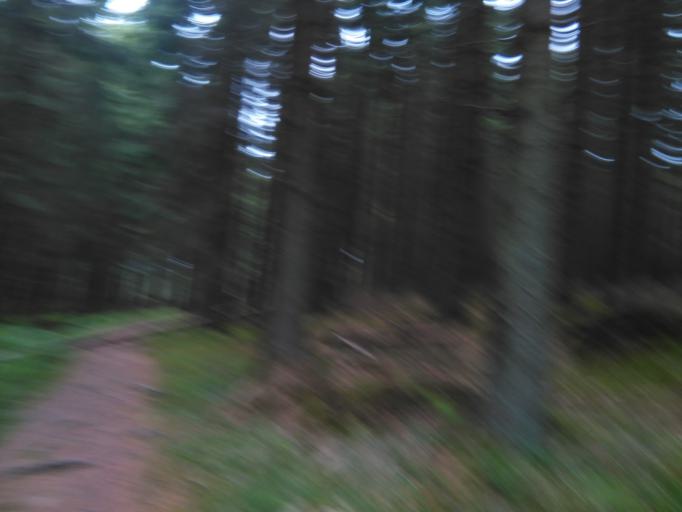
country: DK
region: Capital Region
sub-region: Bornholm Kommune
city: Akirkeby
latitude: 55.1105
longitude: 14.9426
